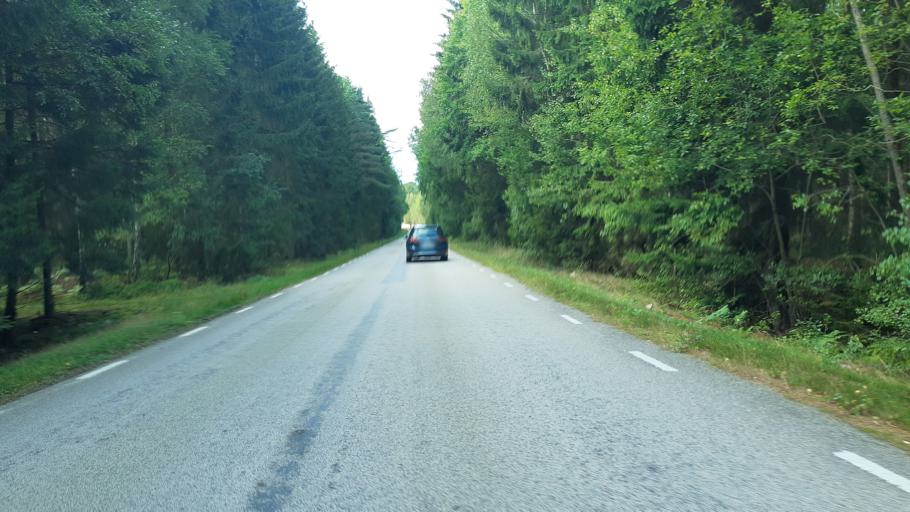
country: SE
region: Blekinge
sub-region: Ronneby Kommun
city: Kallinge
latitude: 56.2218
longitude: 15.3902
